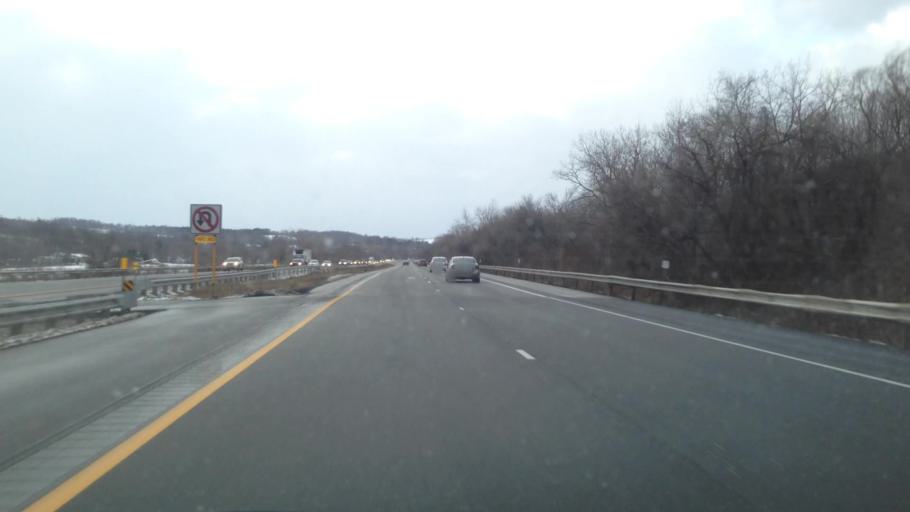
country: US
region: New York
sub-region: Montgomery County
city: Canajoharie
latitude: 42.8939
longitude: -74.5025
